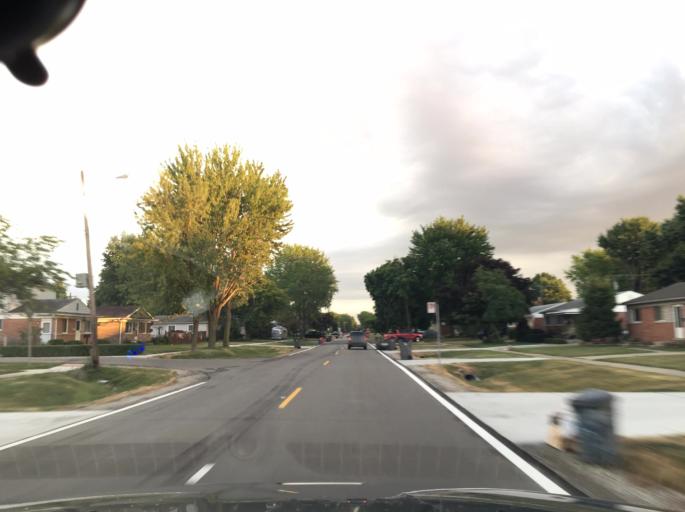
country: US
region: Michigan
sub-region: Macomb County
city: Fraser
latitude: 42.5516
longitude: -82.9202
